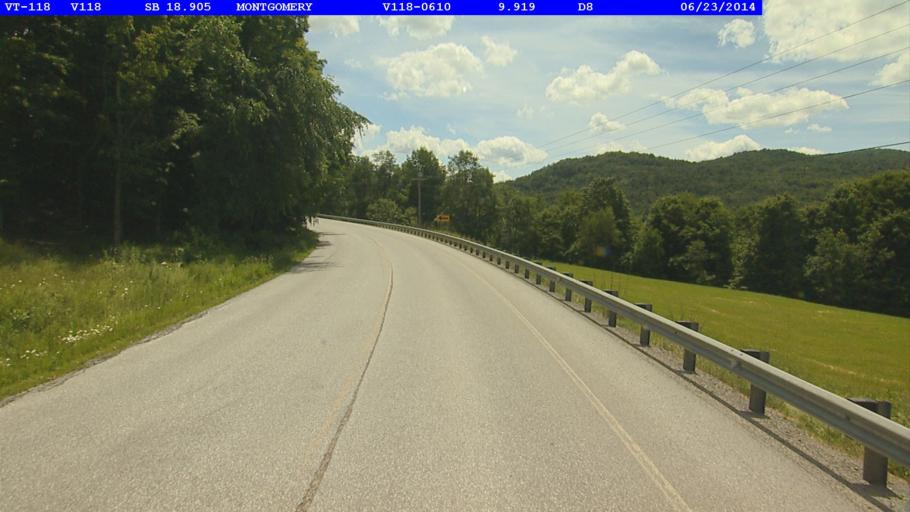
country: US
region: Vermont
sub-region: Franklin County
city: Richford
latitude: 44.9130
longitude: -72.6681
